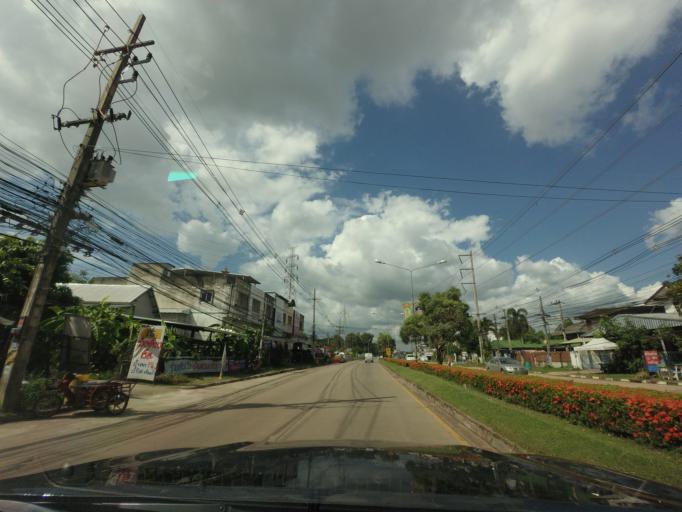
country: TH
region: Changwat Udon Thani
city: Udon Thani
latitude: 17.4326
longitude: 102.7775
